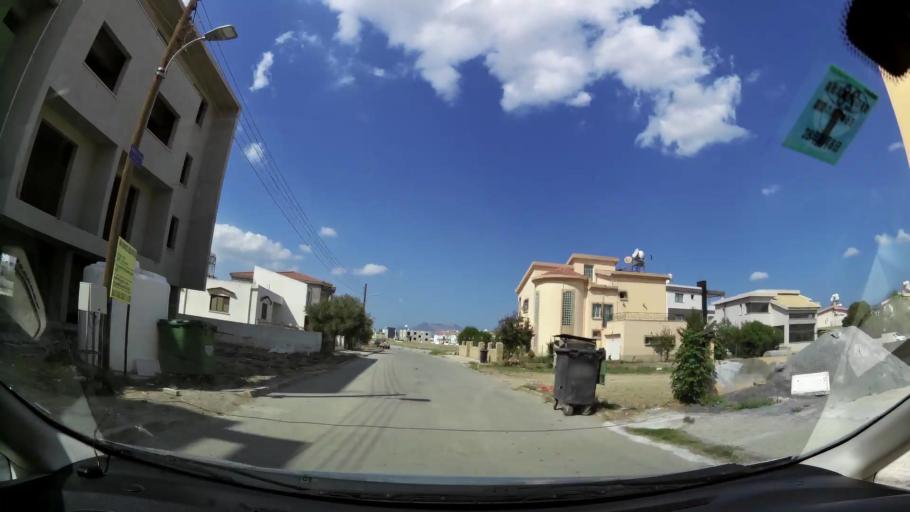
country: CY
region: Lefkosia
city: Nicosia
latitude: 35.2202
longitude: 33.2958
